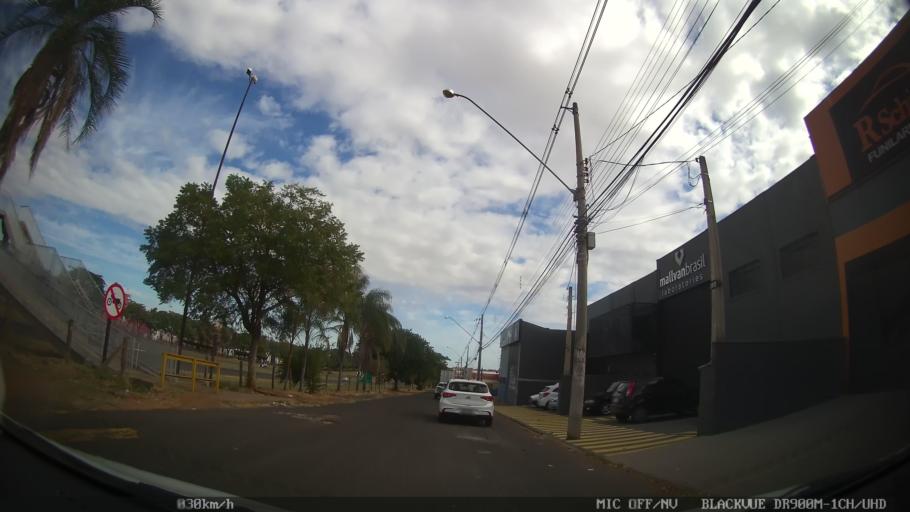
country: BR
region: Sao Paulo
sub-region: Sao Jose Do Rio Preto
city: Sao Jose do Rio Preto
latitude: -20.8094
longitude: -49.4965
